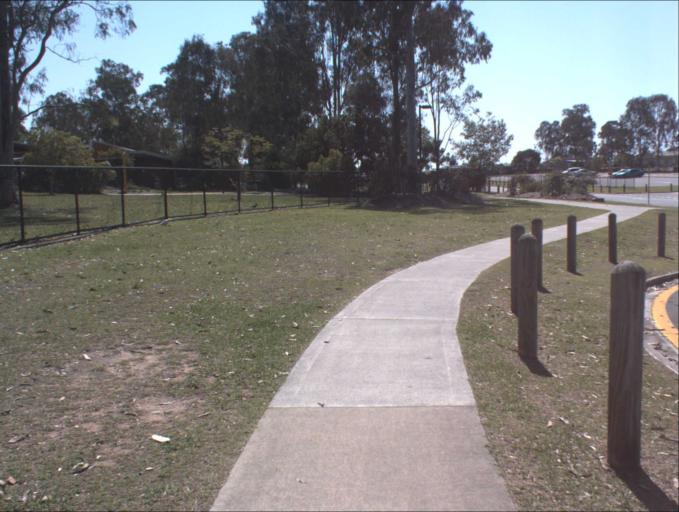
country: AU
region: Queensland
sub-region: Logan
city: North Maclean
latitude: -27.8079
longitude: 152.9559
